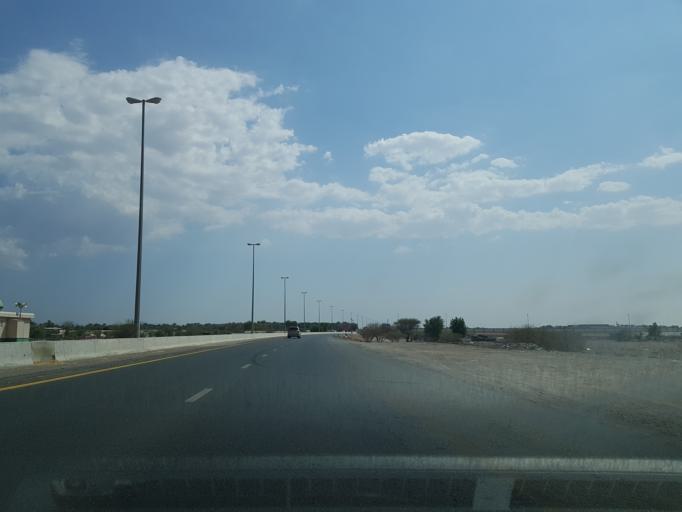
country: AE
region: Ash Shariqah
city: Adh Dhayd
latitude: 25.2398
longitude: 55.9157
